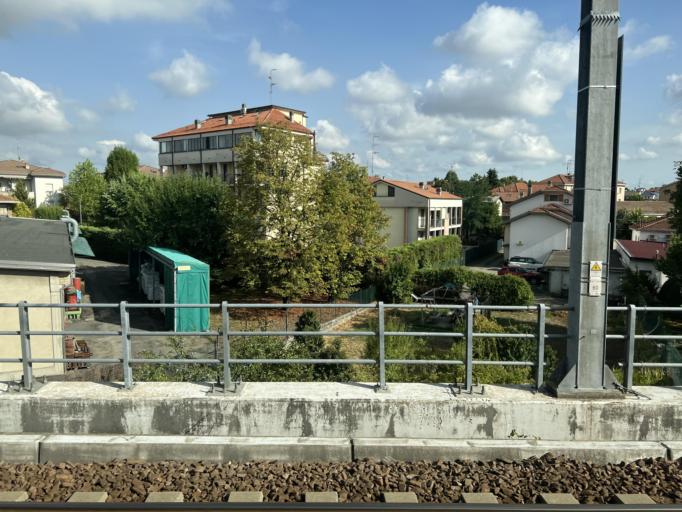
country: IT
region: Emilia-Romagna
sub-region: Provincia di Parma
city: Parma
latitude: 44.8083
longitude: 10.3448
